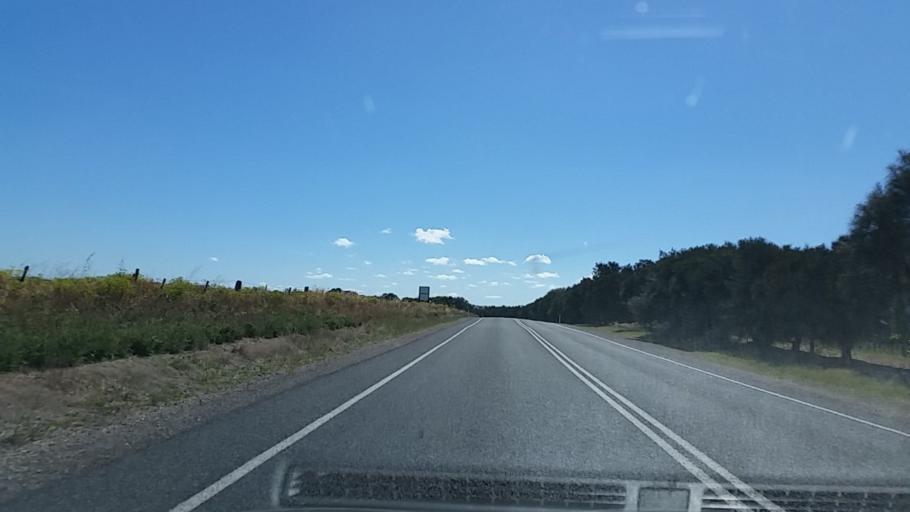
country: AU
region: South Australia
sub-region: Alexandrina
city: Langhorne Creek
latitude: -35.2967
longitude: 138.9674
